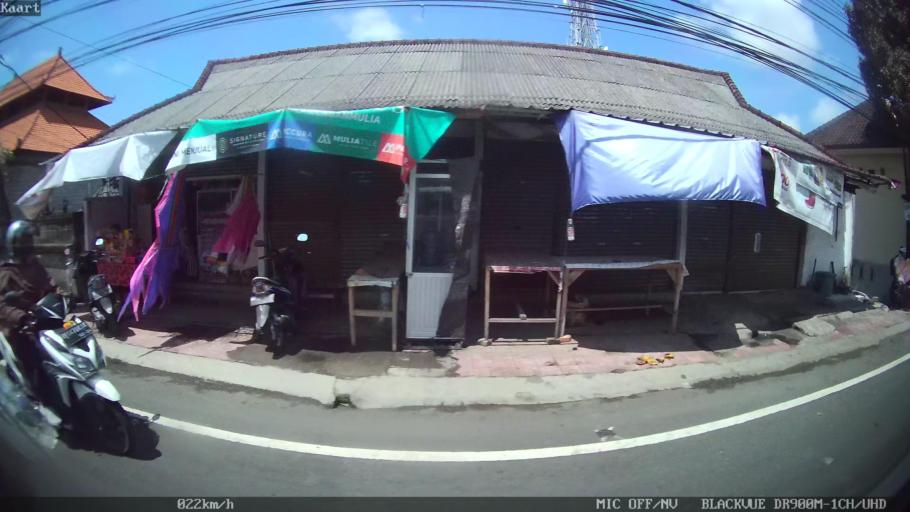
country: ID
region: Bali
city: Banjar Pasekan
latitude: -8.6034
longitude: 115.2763
